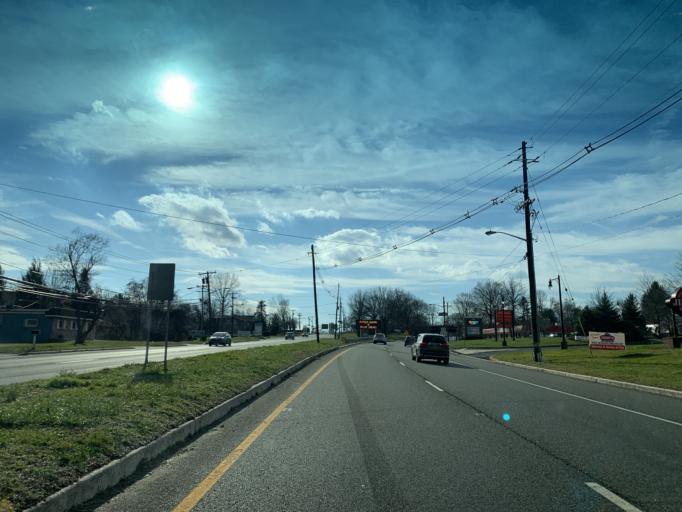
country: US
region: New Jersey
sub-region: Burlington County
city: Bordentown
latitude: 40.1548
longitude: -74.6972
